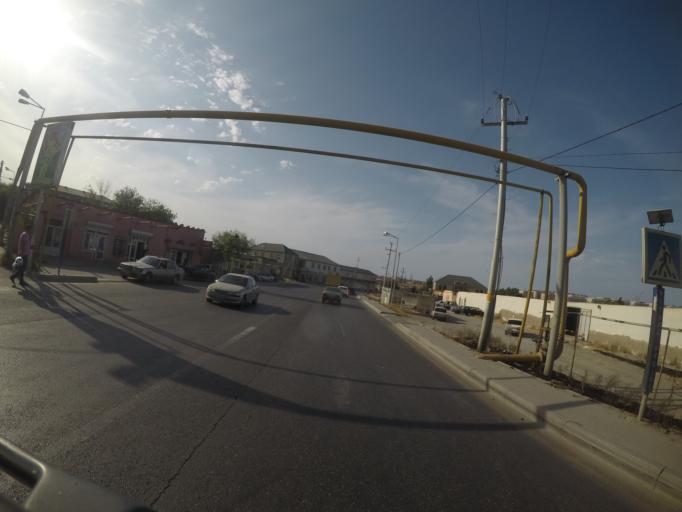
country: AZ
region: Baki
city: Binagadi
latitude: 40.4758
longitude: 49.8333
